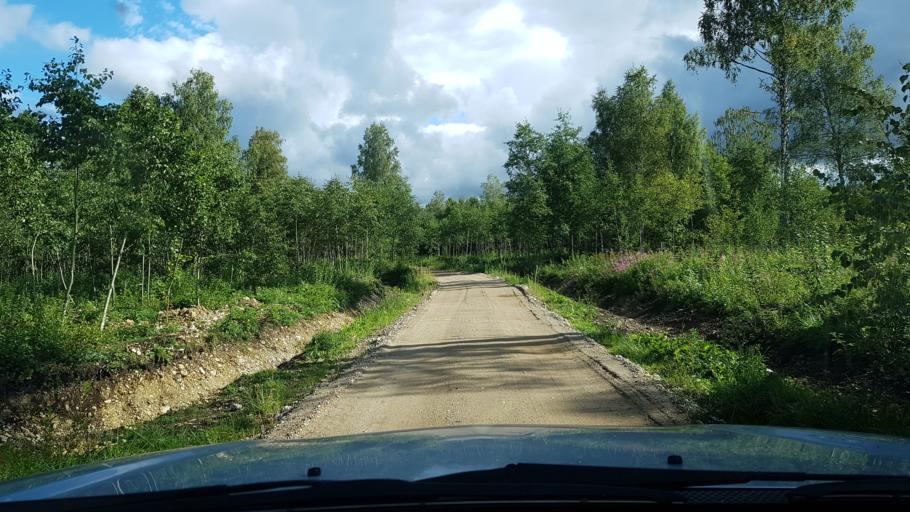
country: EE
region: Harju
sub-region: Raasiku vald
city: Arukula
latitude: 59.2543
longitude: 25.0987
